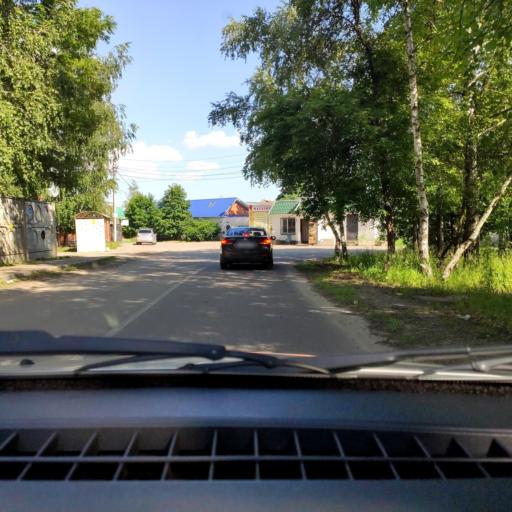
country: RU
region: Voronezj
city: Ramon'
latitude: 51.8218
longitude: 39.2663
